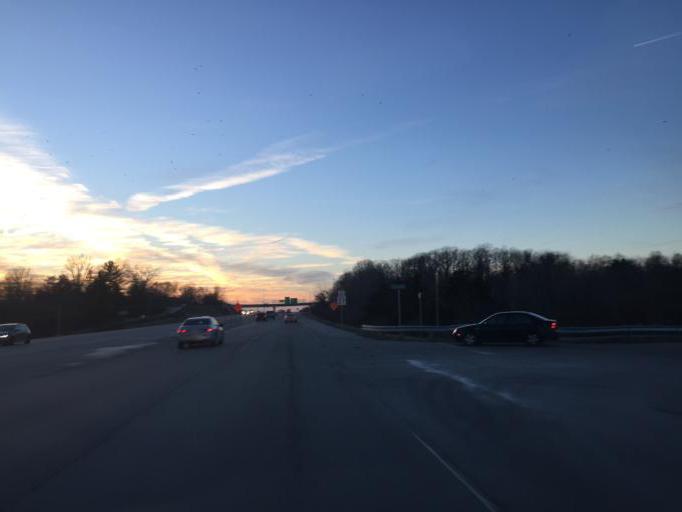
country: US
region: Indiana
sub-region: Monroe County
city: Bloomington
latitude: 39.1869
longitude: -86.5463
